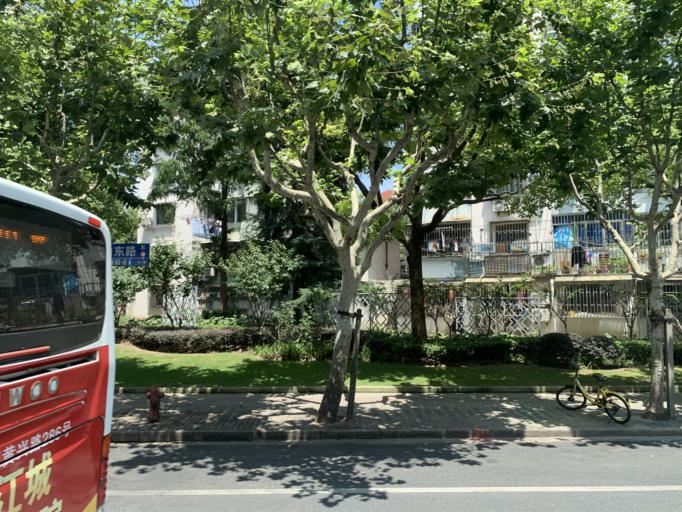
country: CN
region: Shanghai Shi
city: Pudong
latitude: 31.2499
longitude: 121.5563
